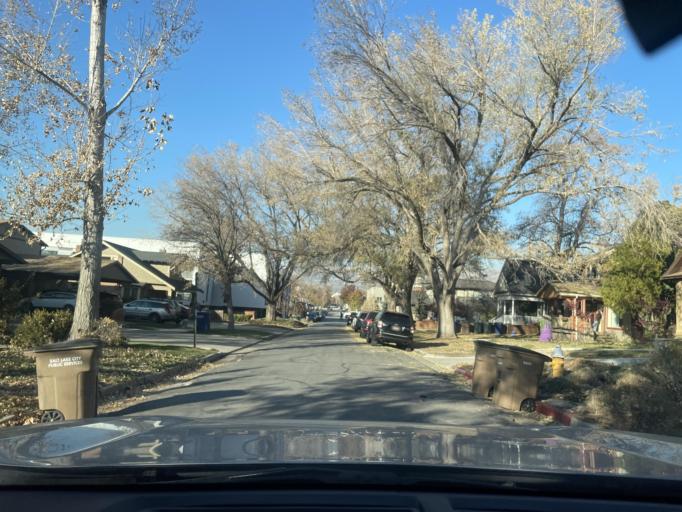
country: US
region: Utah
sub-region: Salt Lake County
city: Salt Lake City
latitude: 40.7485
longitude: -111.8639
